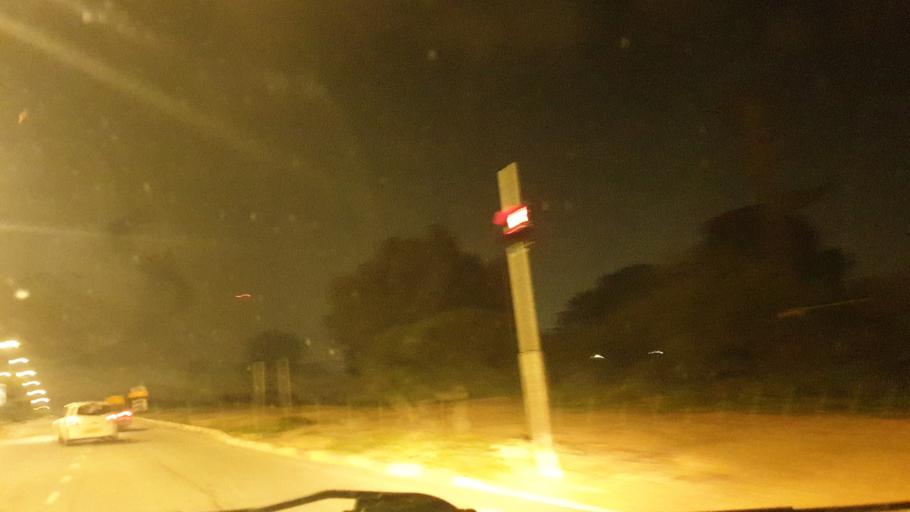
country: IL
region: Central District
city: Bet Dagan
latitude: 31.9678
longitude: 34.8271
